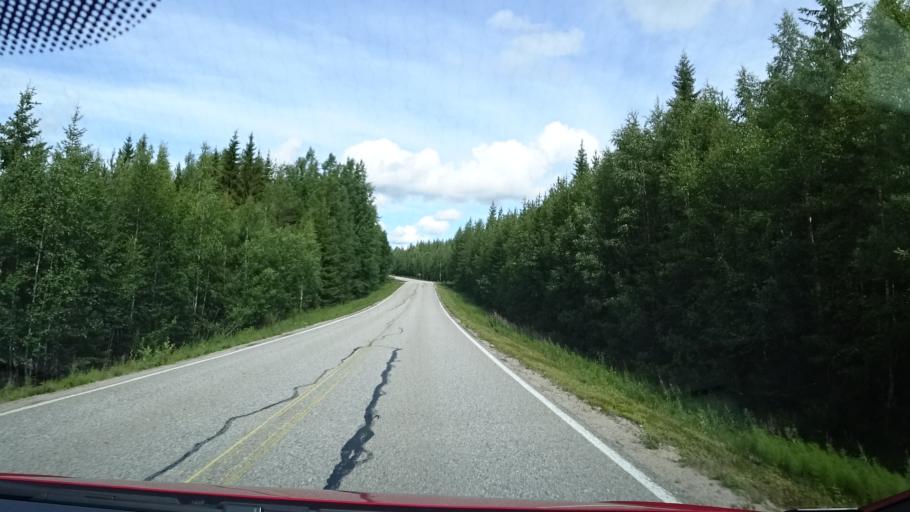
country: FI
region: Kainuu
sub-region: Kehys-Kainuu
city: Kuhmo
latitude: 64.4308
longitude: 29.8115
